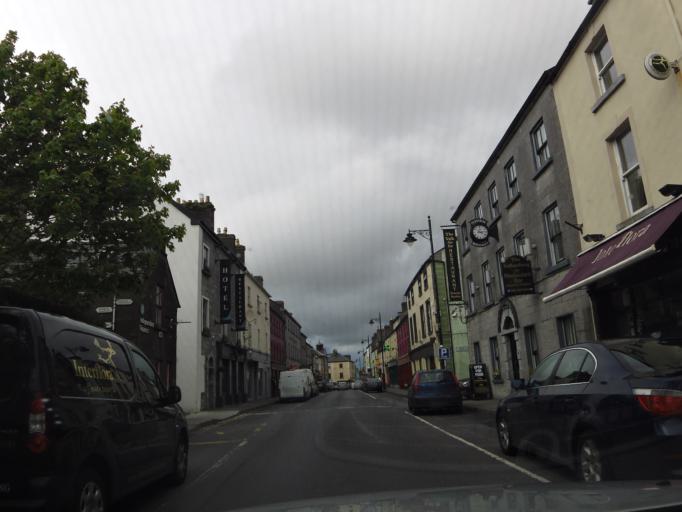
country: IE
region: Connaught
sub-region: Maigh Eo
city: Ballinrobe
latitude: 53.6226
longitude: -9.2229
